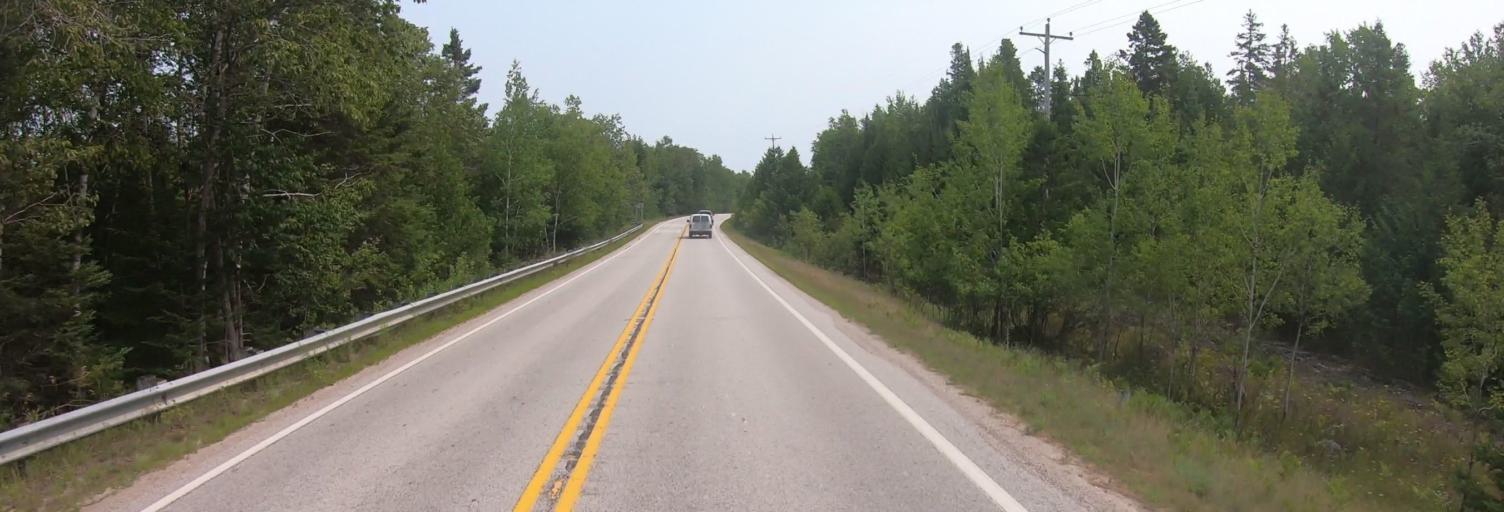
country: CA
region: Ontario
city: Thessalon
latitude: 45.9940
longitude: -83.8678
